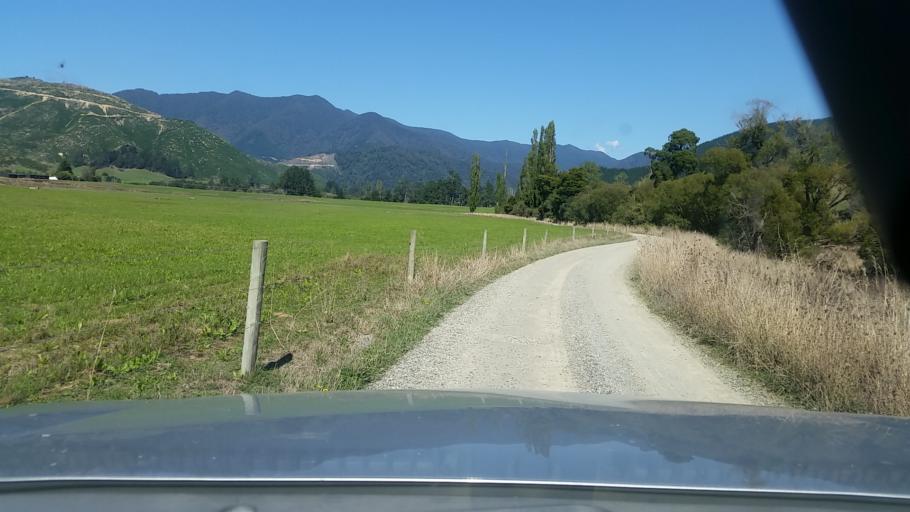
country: NZ
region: Nelson
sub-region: Nelson City
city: Nelson
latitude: -41.2661
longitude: 173.5763
